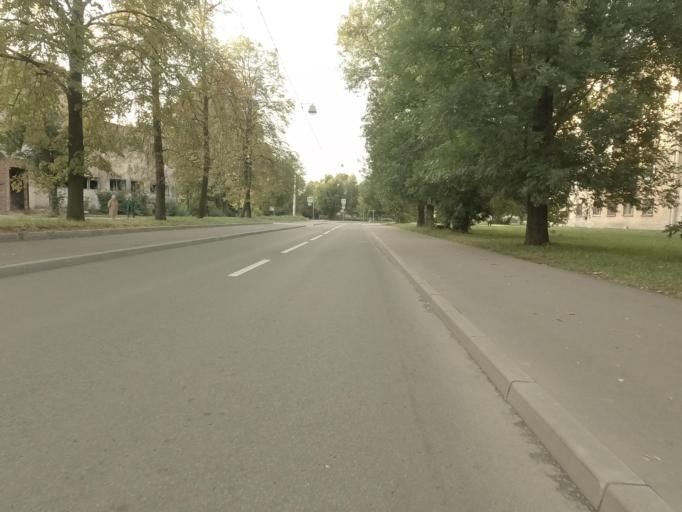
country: RU
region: St.-Petersburg
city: Admiralteisky
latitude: 59.8934
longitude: 30.2698
